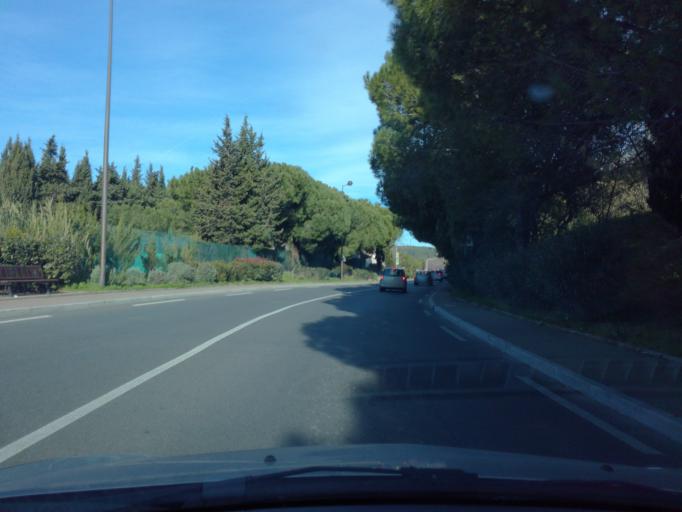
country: FR
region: Provence-Alpes-Cote d'Azur
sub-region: Departement des Alpes-Maritimes
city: Vallauris
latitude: 43.5750
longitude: 7.0903
